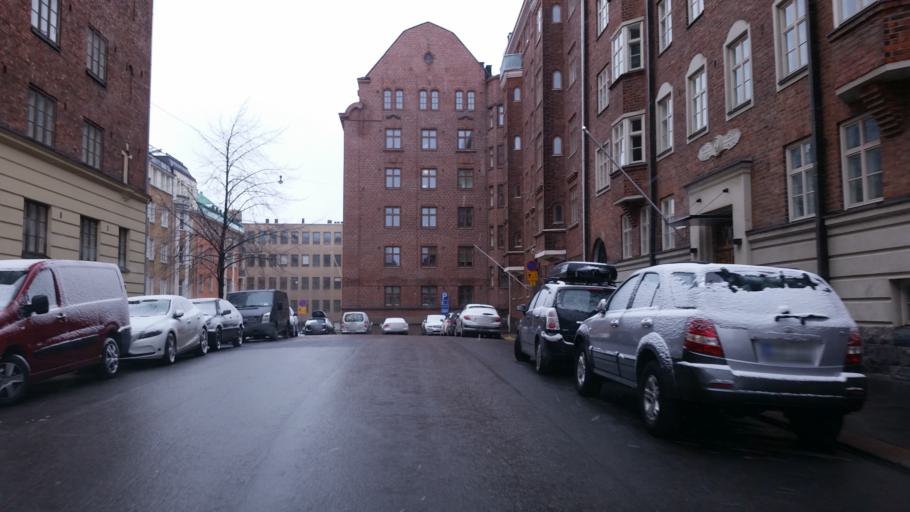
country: FI
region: Uusimaa
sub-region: Helsinki
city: Helsinki
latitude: 60.1742
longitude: 24.9259
